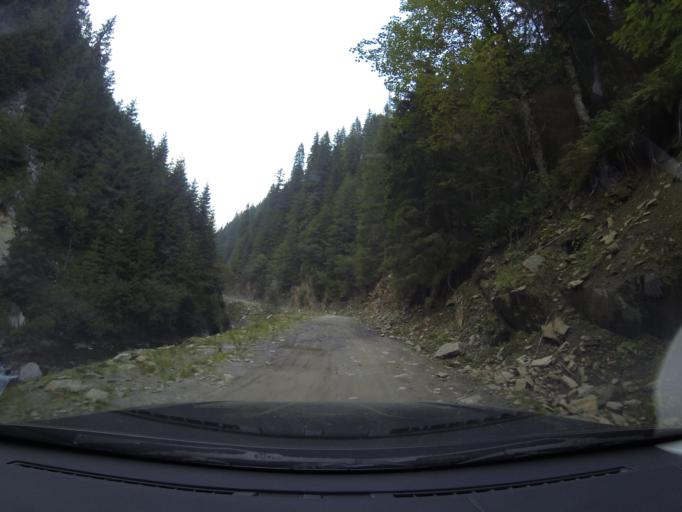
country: RO
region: Brasov
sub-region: Oras Victoria
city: Victoria
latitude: 45.5340
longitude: 24.6775
